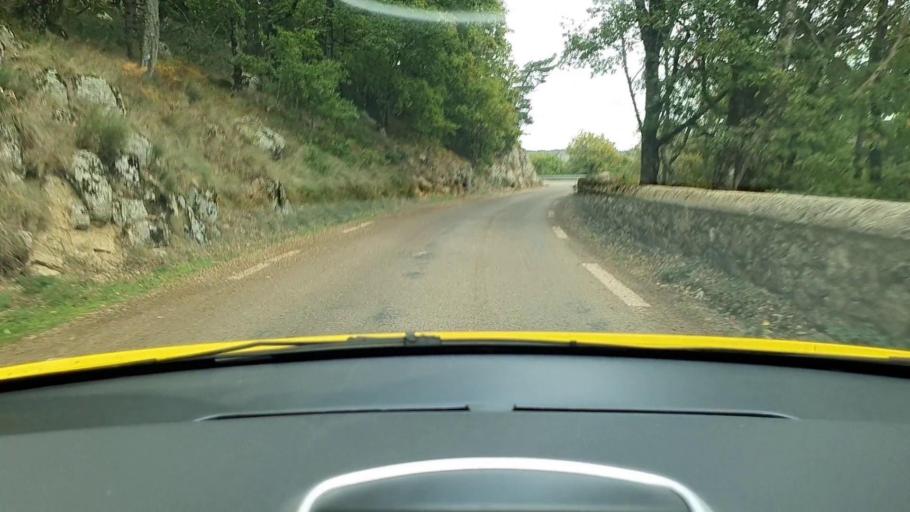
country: FR
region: Languedoc-Roussillon
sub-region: Departement du Gard
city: Le Vigan
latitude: 44.0341
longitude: 3.5722
